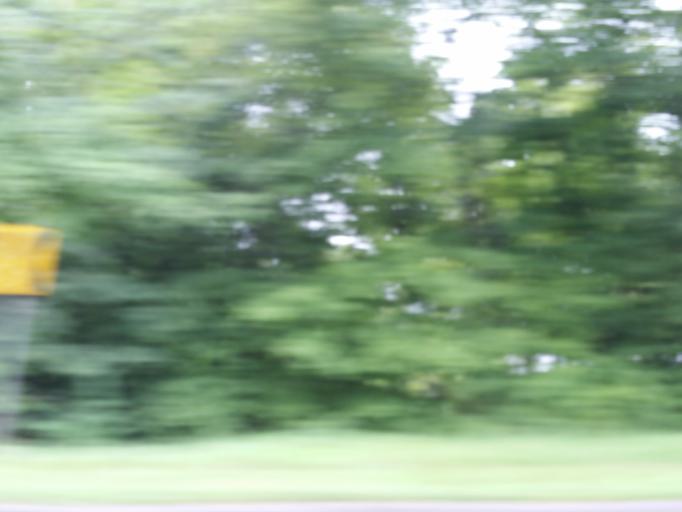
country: US
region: Missouri
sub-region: Cape Girardeau County
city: Cape Girardeau
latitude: 37.3548
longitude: -89.5626
